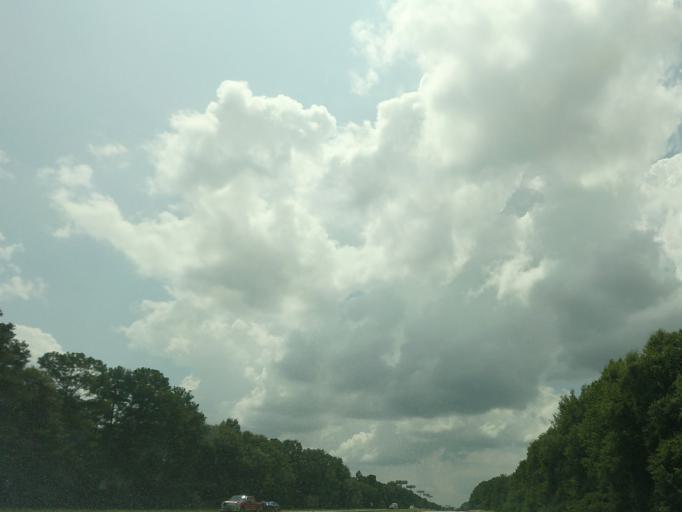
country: US
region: Georgia
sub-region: Peach County
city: Byron
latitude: 32.6412
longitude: -83.7438
